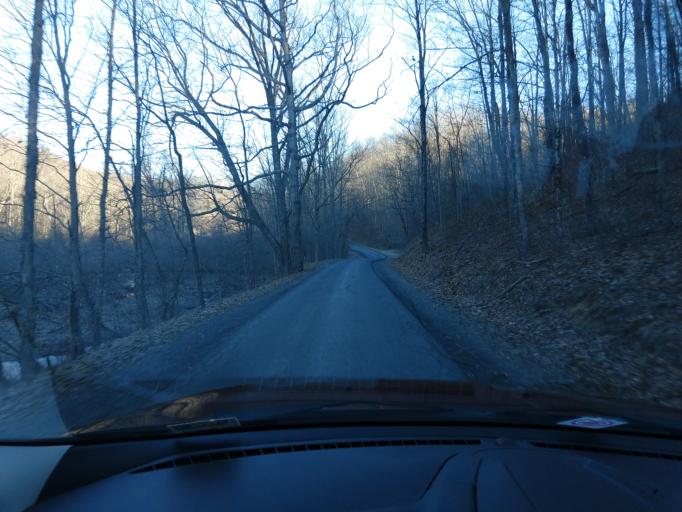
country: US
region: West Virginia
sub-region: Greenbrier County
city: Rainelle
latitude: 37.8902
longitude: -80.7297
